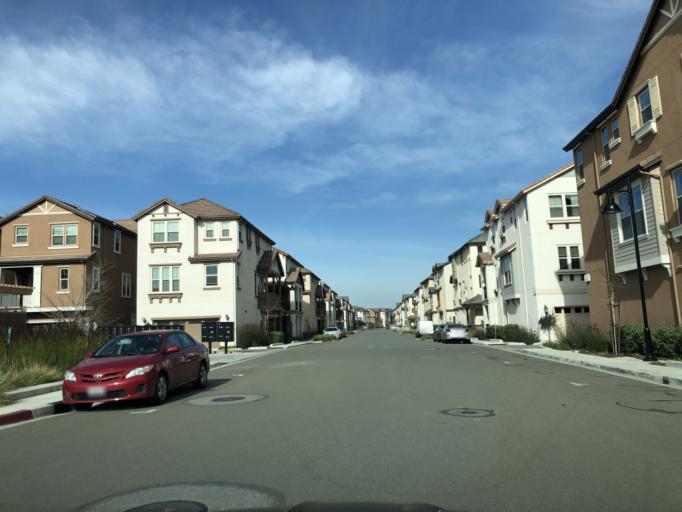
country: US
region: California
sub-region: Santa Clara County
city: Milpitas
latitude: 37.4503
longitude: -121.9186
